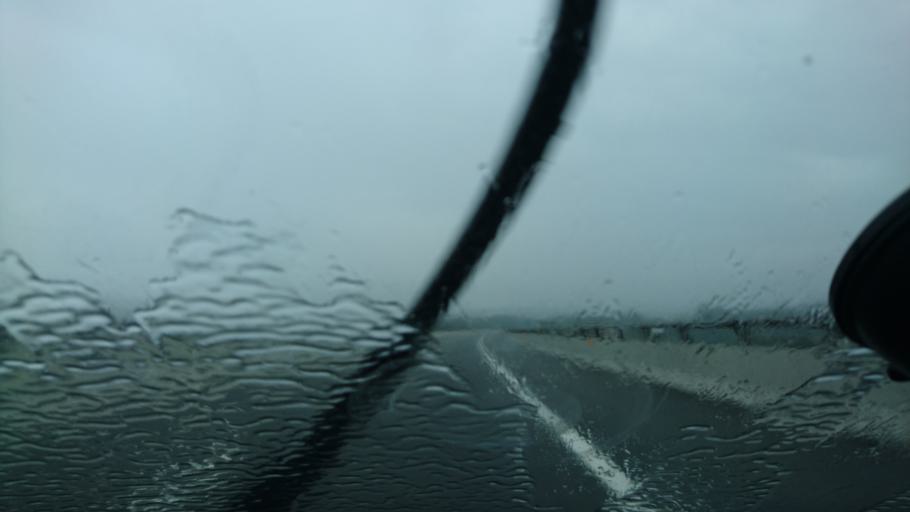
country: IT
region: Piedmont
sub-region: Provincia di Novara
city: Fontaneto D'Agogna
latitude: 45.6517
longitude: 8.4707
